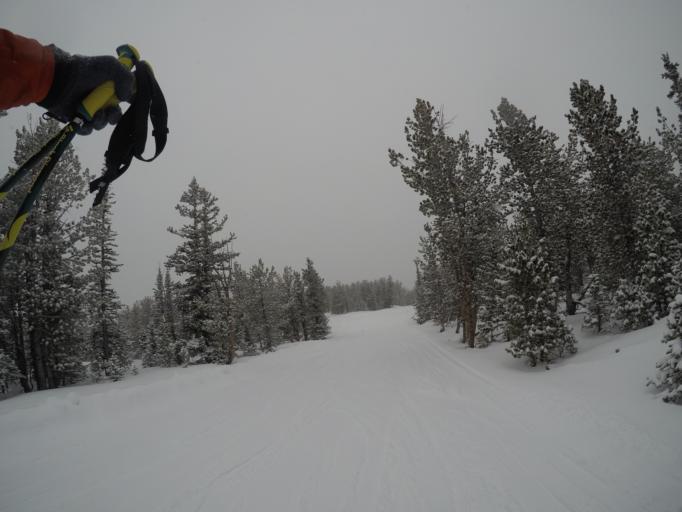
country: US
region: Montana
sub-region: Carbon County
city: Red Lodge
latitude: 45.1834
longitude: -109.3585
